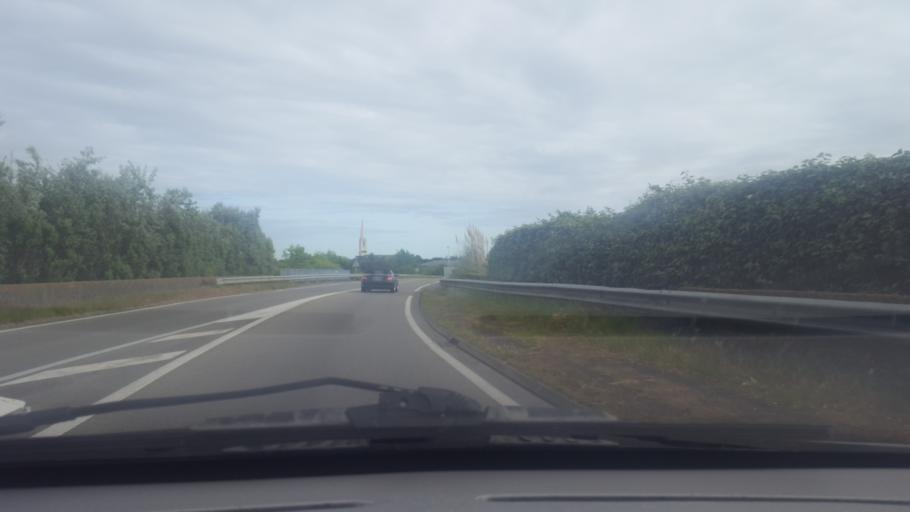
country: FR
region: Pays de la Loire
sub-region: Departement de la Loire-Atlantique
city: Bourgneuf-en-Retz
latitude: 47.0474
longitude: -1.9582
